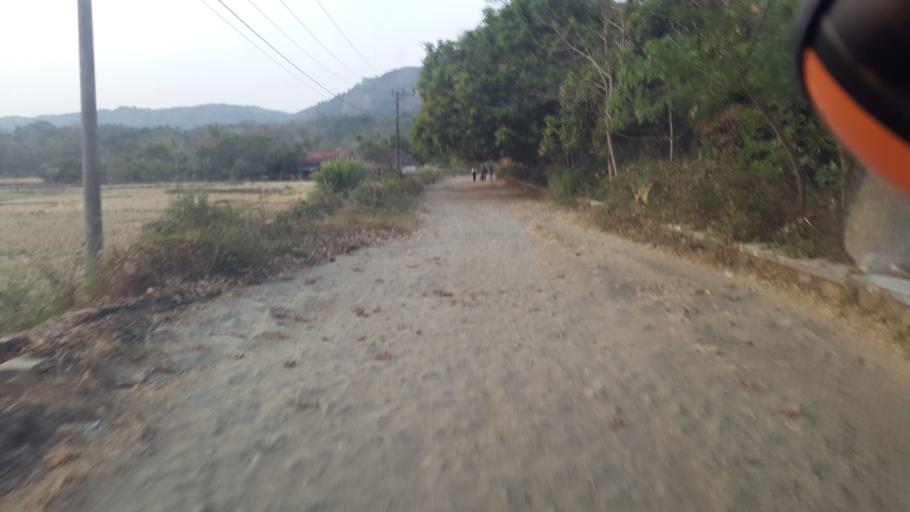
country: ID
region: West Java
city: Ciemas
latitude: -7.2173
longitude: 106.5006
